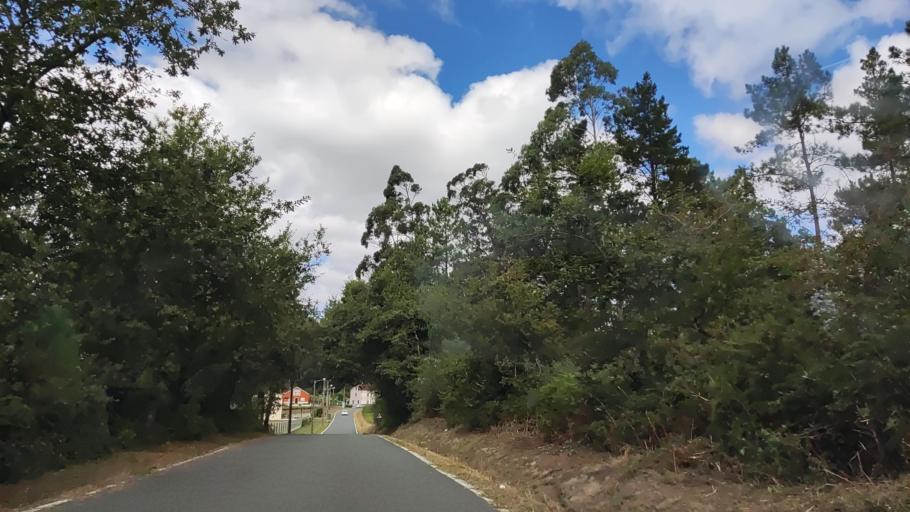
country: ES
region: Galicia
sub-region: Provincia da Coruna
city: Rois
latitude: 42.7525
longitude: -8.7022
